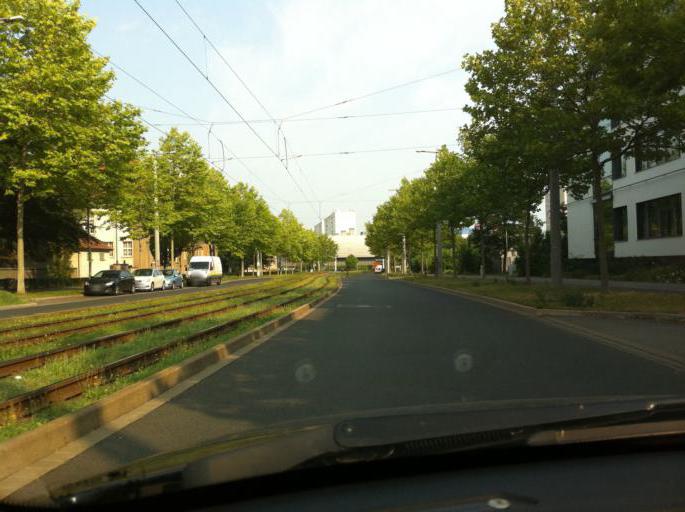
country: DE
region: Saxony
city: Leipzig
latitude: 51.3205
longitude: 12.3943
